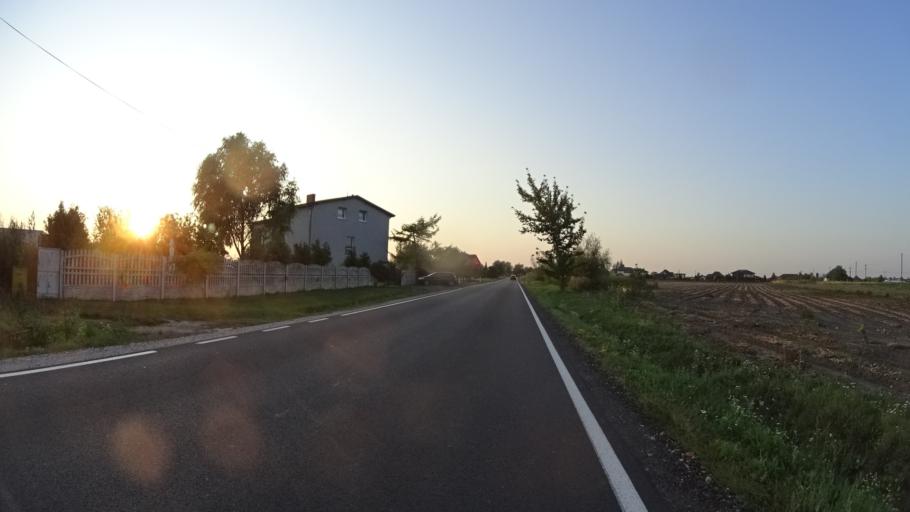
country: PL
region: Masovian Voivodeship
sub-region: Powiat warszawski zachodni
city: Ozarow Mazowiecki
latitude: 52.2430
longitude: 20.7488
